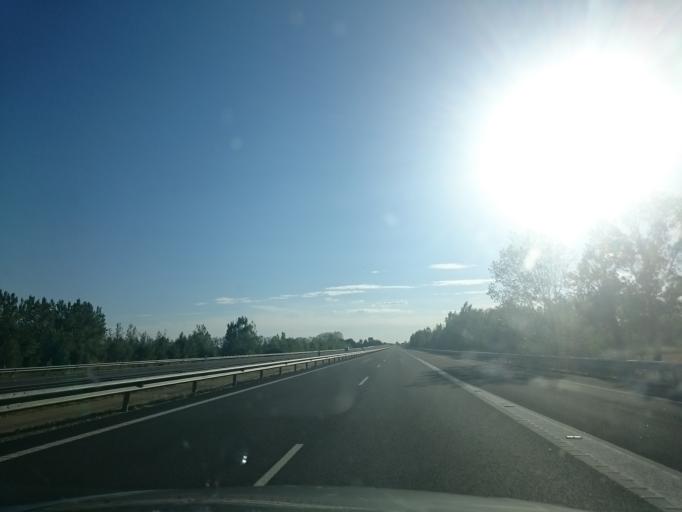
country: ES
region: Castille and Leon
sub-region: Provincia de Burgos
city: Sasamon
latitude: 42.3950
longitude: -4.0758
